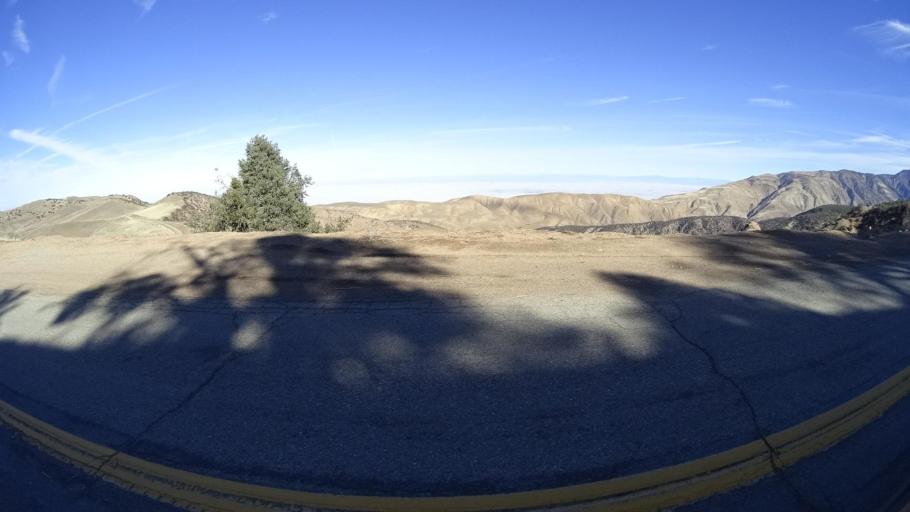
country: US
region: California
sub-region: Kern County
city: Maricopa
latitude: 34.8792
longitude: -119.3524
